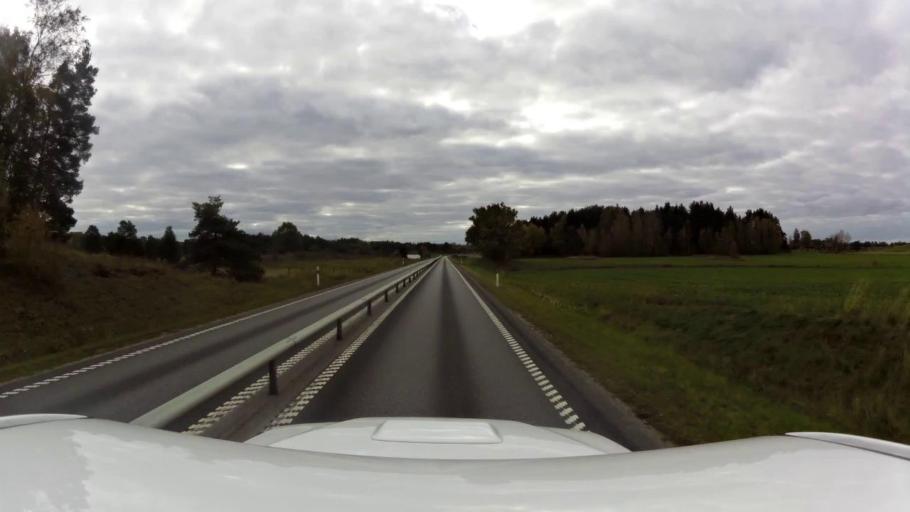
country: SE
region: OEstergoetland
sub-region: Linkopings Kommun
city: Malmslatt
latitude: 58.3269
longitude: 15.5648
